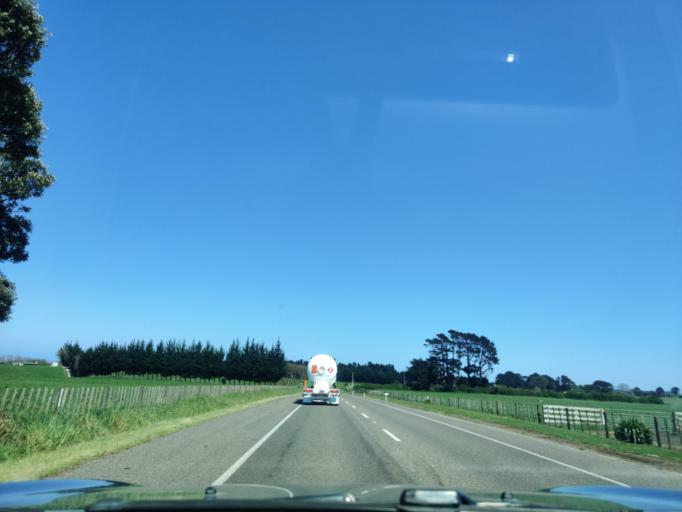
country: NZ
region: Manawatu-Wanganui
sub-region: Wanganui District
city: Wanganui
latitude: -39.8225
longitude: 174.8520
